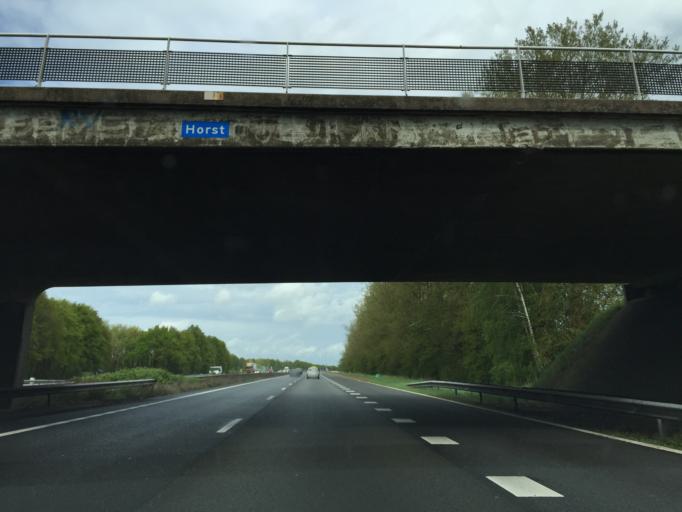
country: NL
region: Gelderland
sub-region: Gemeente Ermelo
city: Horst
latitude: 52.3118
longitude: 5.5631
